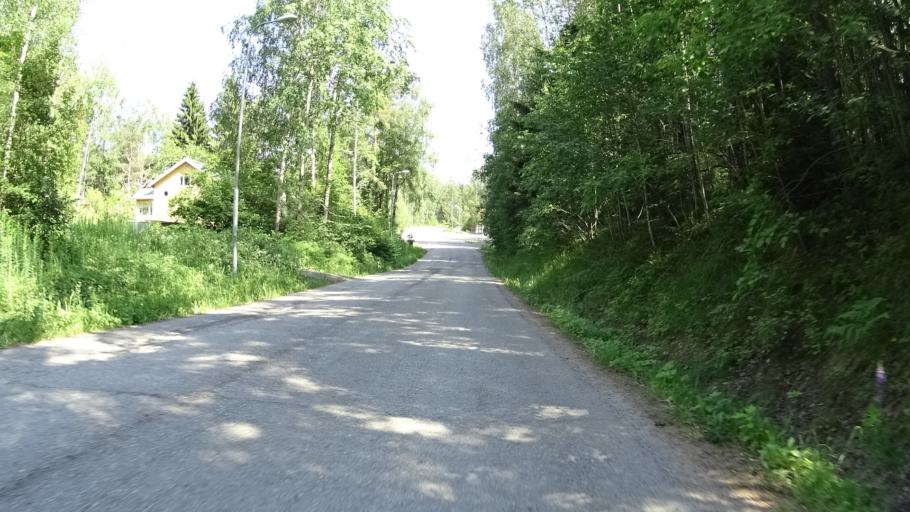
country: FI
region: Uusimaa
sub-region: Raaseporin
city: Karis
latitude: 60.0824
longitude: 23.6596
